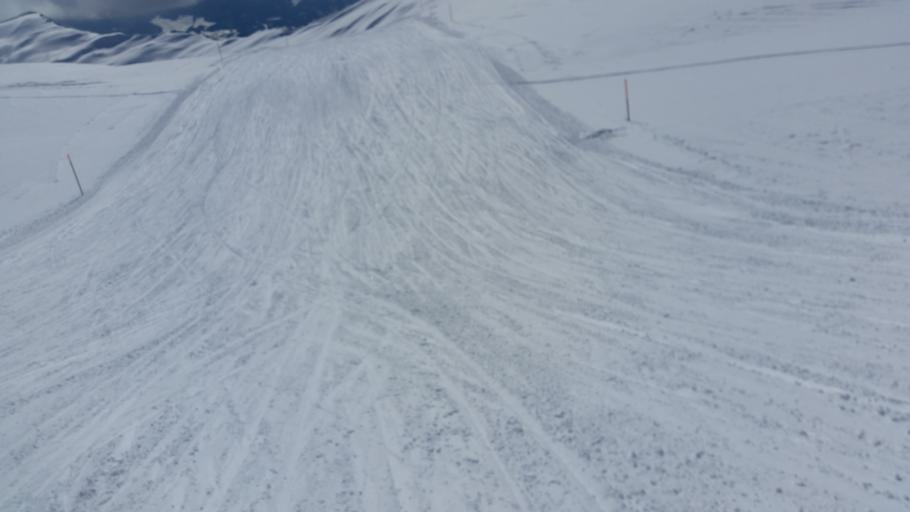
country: CH
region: Grisons
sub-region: Surselva District
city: Ilanz
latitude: 46.8605
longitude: 9.1569
